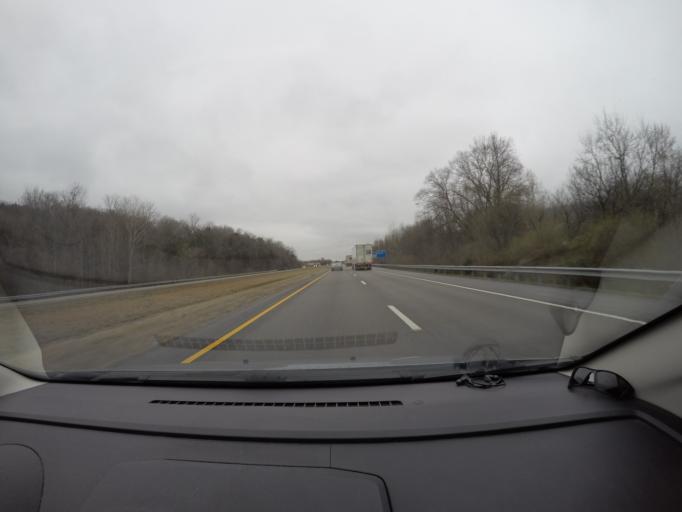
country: US
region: Tennessee
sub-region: Marion County
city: South Pittsburg
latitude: 35.0569
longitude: -85.7193
